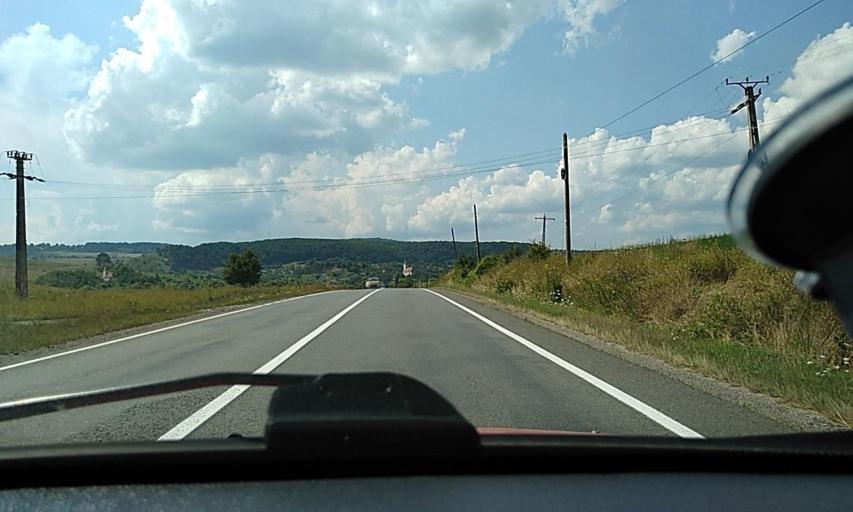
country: RO
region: Brasov
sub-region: Comuna Bunesti
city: Bunesti
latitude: 46.1122
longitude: 25.0545
